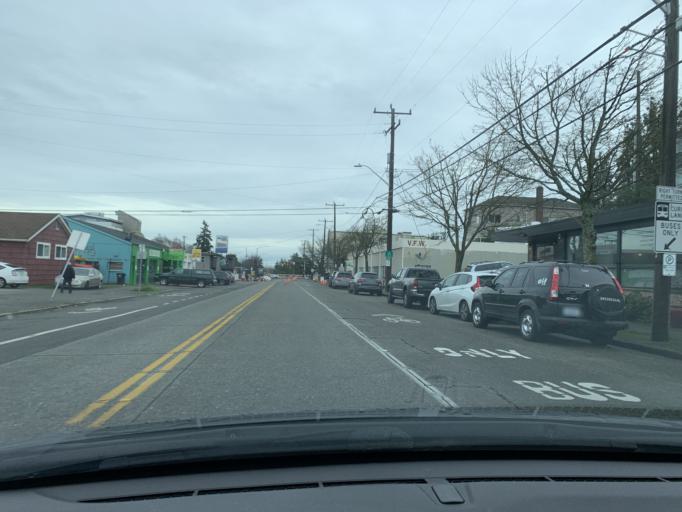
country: US
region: Washington
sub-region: King County
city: White Center
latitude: 47.5610
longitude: -122.3790
